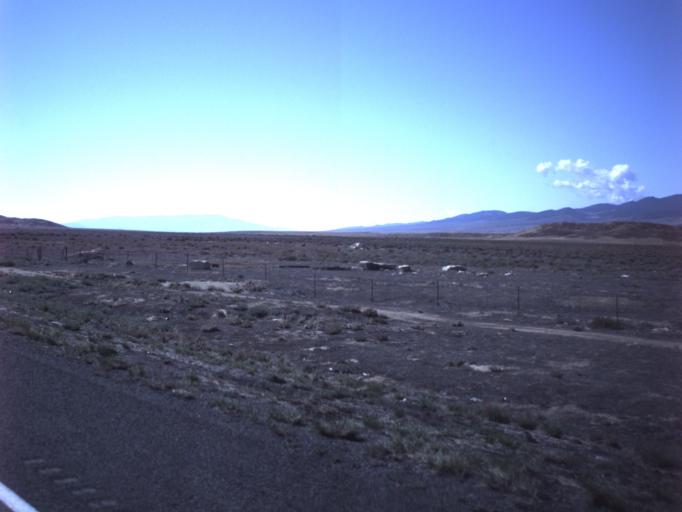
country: US
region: Utah
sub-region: Sanpete County
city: Gunnison
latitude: 39.1856
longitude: -111.8410
